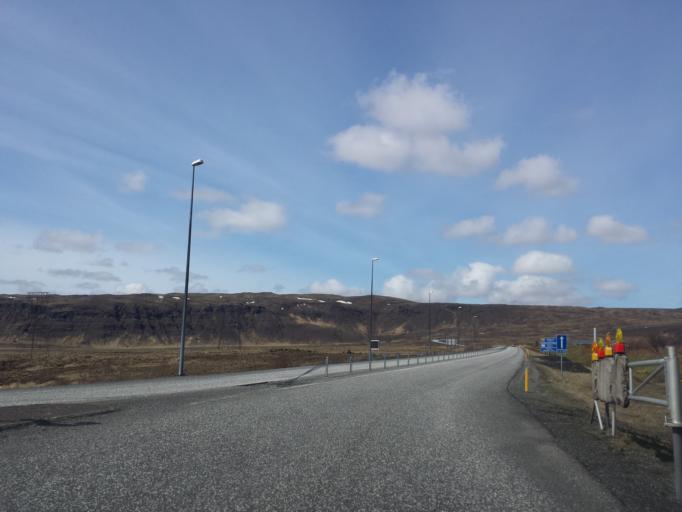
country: IS
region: South
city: Hveragerdi
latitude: 63.9954
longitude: -21.1933
